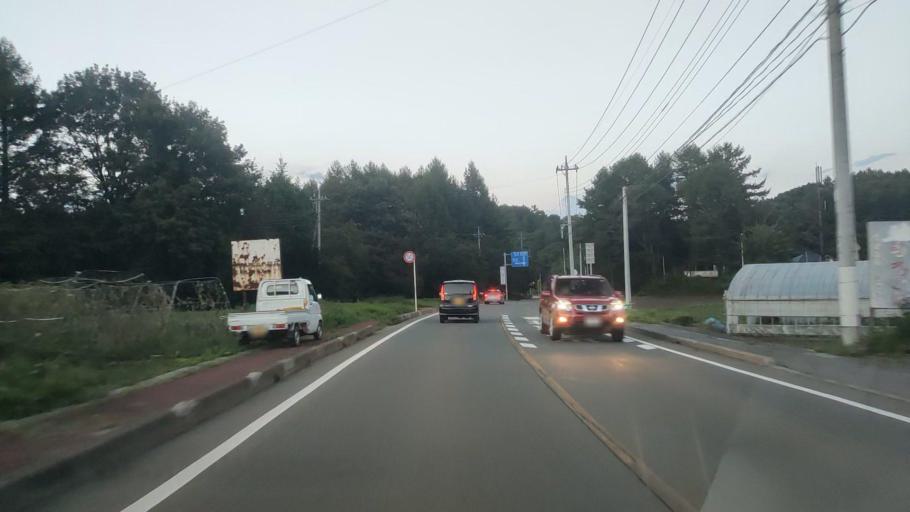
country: JP
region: Nagano
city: Komoro
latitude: 36.5112
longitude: 138.5947
